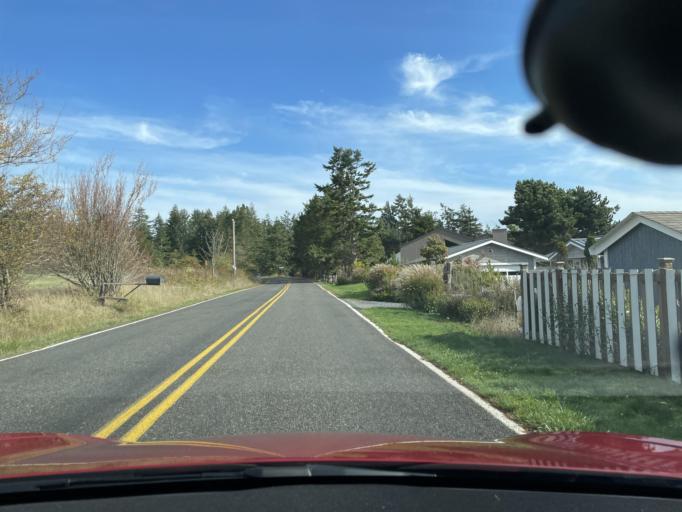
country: US
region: Washington
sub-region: San Juan County
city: Friday Harbor
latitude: 48.5201
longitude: -122.9776
